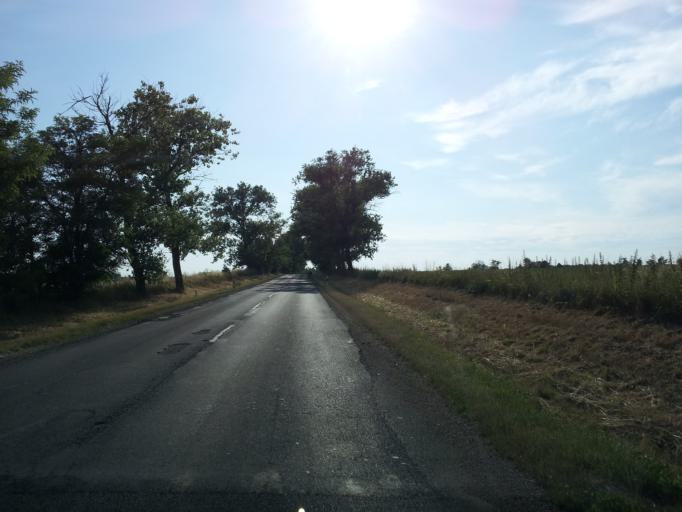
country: HU
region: Veszprem
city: Urkut
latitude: 46.9886
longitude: 17.7140
